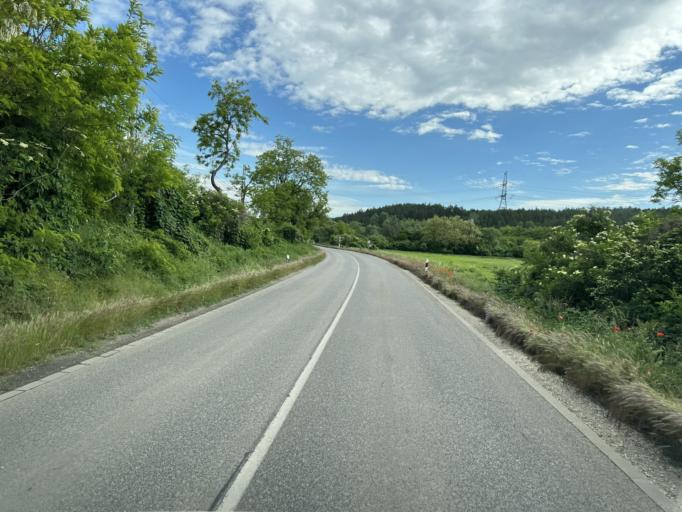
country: HU
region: Pest
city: Pecel
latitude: 47.4971
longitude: 19.3708
